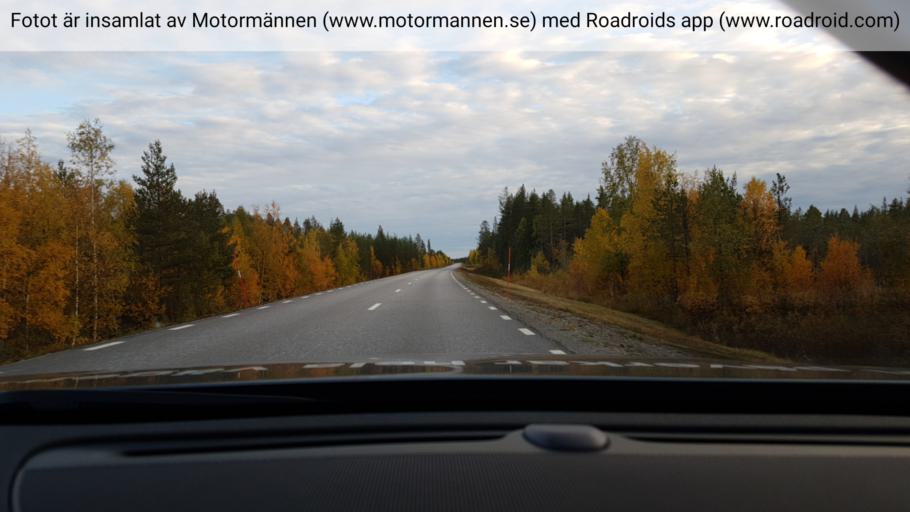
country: SE
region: Norrbotten
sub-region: Jokkmokks Kommun
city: Jokkmokk
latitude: 66.4160
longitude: 19.6874
